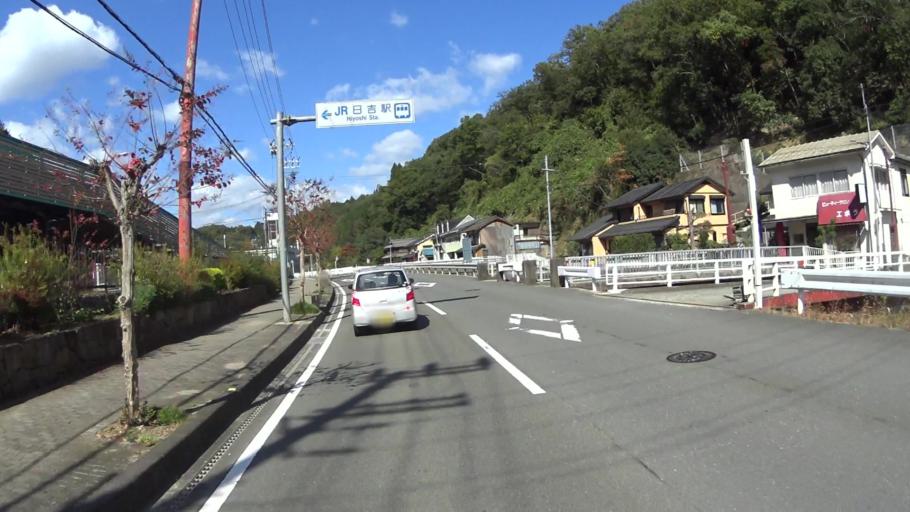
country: JP
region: Kyoto
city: Kameoka
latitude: 35.1623
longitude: 135.5039
